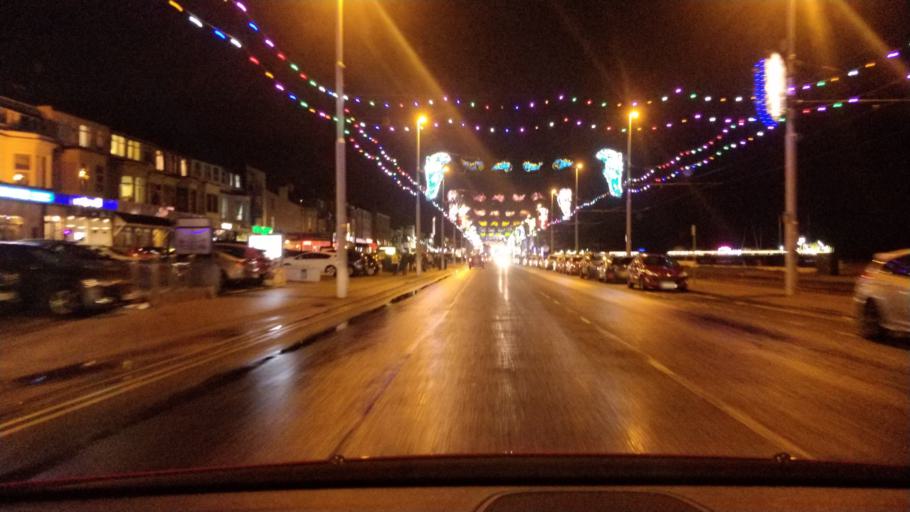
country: GB
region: England
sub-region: Blackpool
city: Blackpool
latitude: 53.8020
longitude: -3.0554
